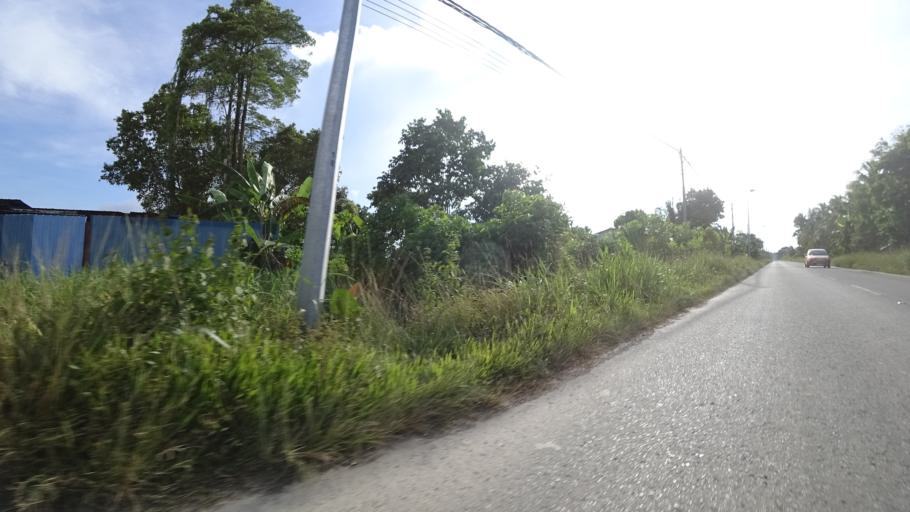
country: BN
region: Brunei and Muara
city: Bandar Seri Begawan
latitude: 4.8441
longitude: 114.8524
